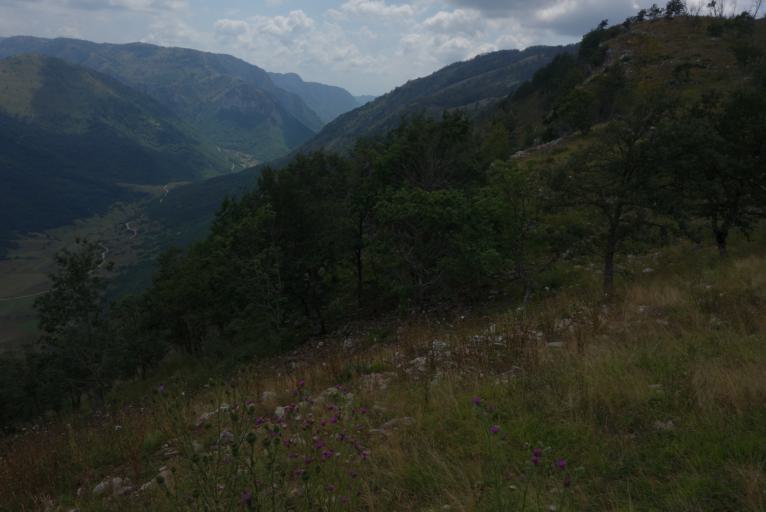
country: AL
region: Lezhe
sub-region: Rrethi i Mirdites
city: Orosh
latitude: 41.8437
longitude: 20.1553
